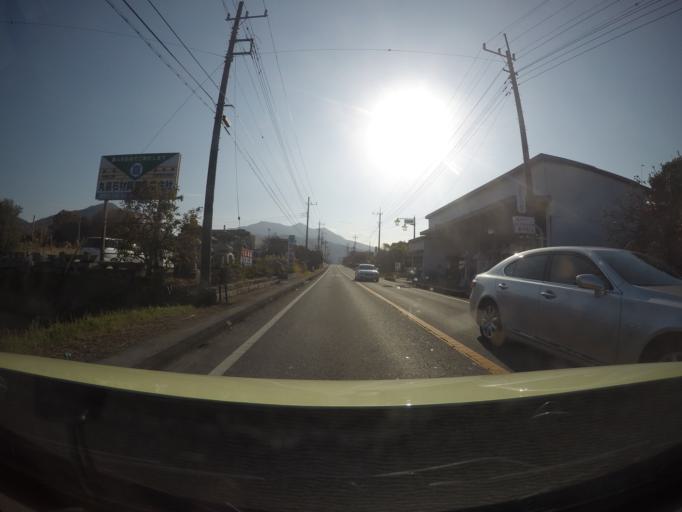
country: JP
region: Ibaraki
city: Makabe
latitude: 36.2771
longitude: 140.1071
